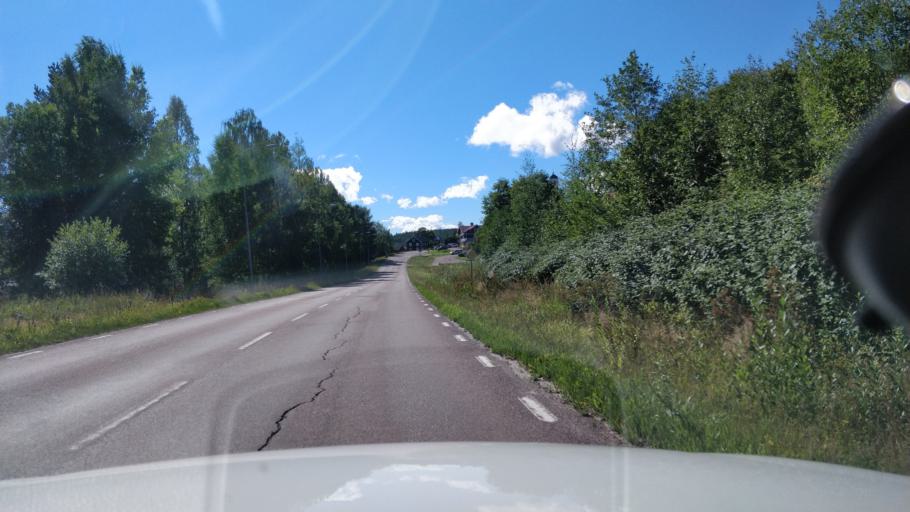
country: SE
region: Dalarna
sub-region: Faluns Kommun
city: Bjursas
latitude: 60.7374
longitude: 15.4577
